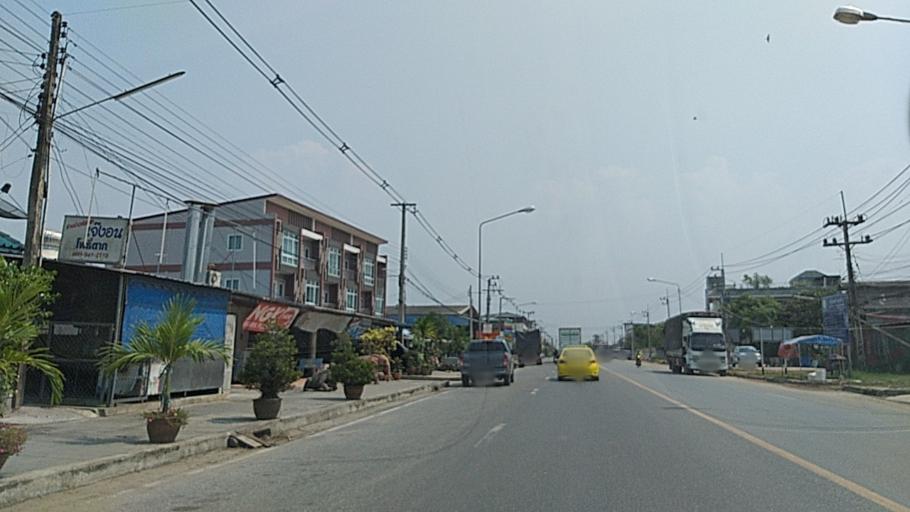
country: TH
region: Chon Buri
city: Phanat Nikhom
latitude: 13.4370
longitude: 101.1798
